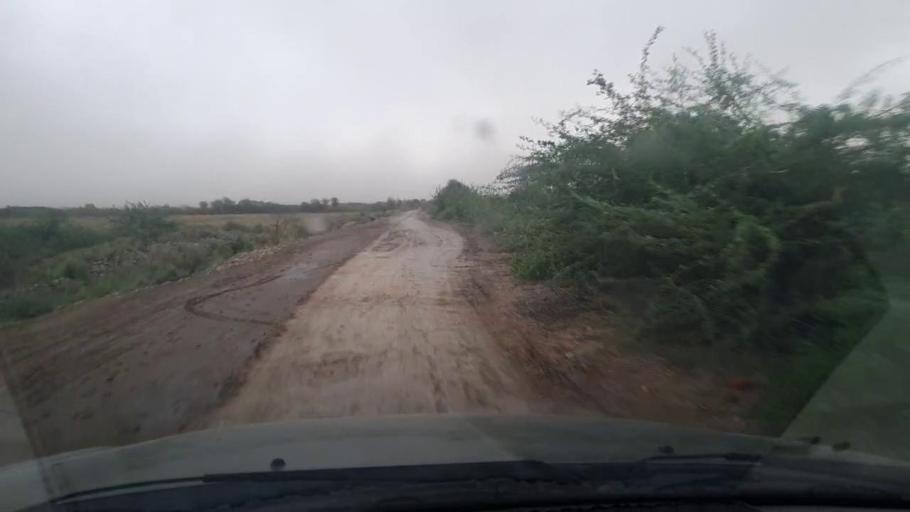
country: PK
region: Sindh
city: Digri
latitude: 24.9971
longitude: 69.0485
